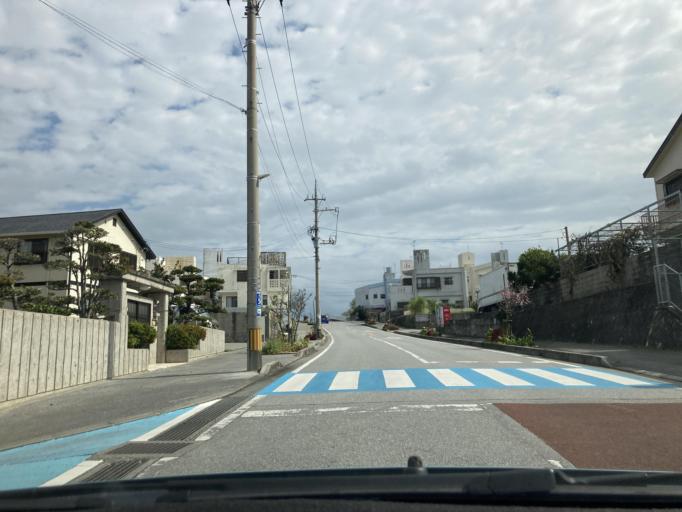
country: JP
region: Okinawa
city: Tomigusuku
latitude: 26.1858
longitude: 127.6930
